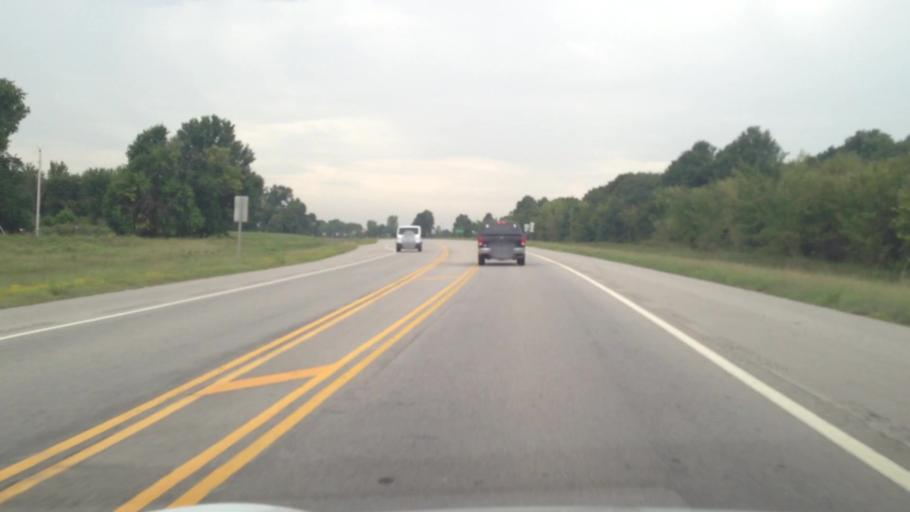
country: US
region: Kansas
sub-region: Cherokee County
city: Baxter Springs
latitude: 37.0583
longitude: -94.7338
